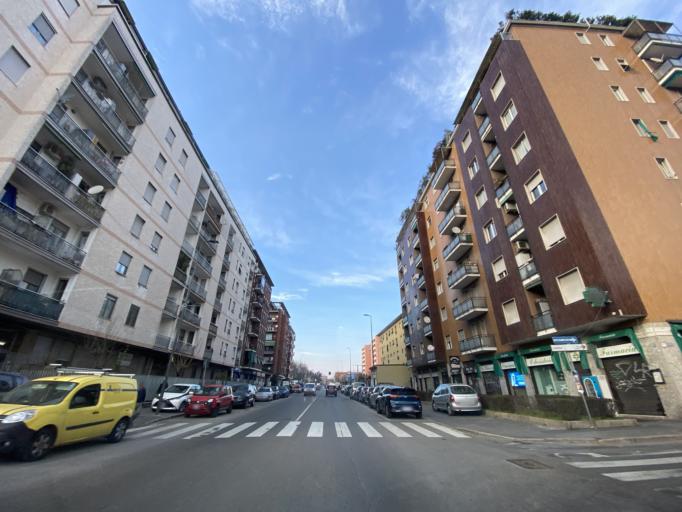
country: IT
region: Lombardy
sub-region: Citta metropolitana di Milano
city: Novate Milanese
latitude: 45.5130
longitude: 9.1368
